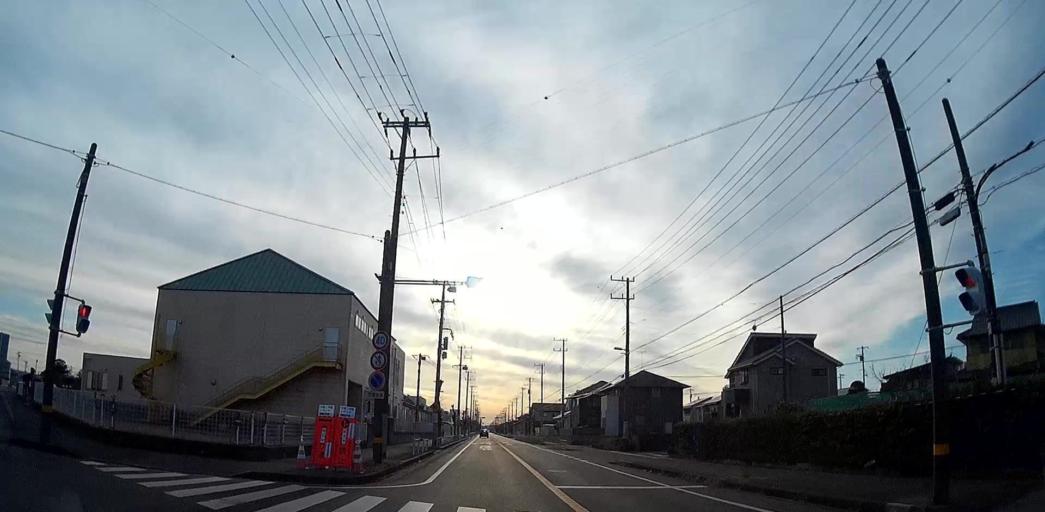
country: JP
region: Chiba
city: Hasaki
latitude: 35.7981
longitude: 140.7788
